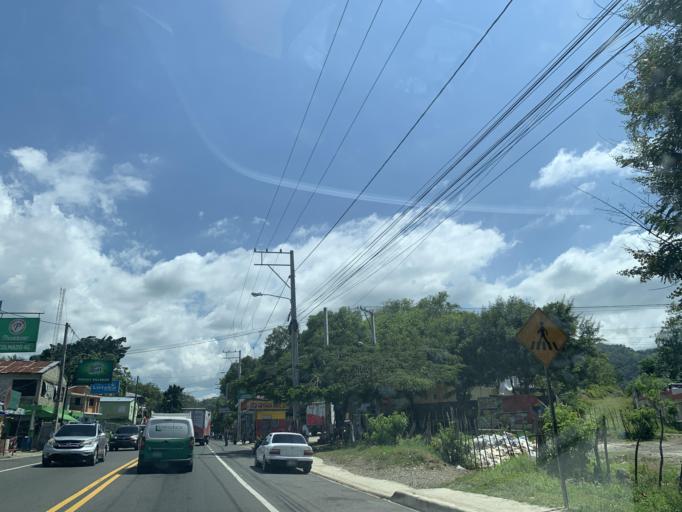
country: DO
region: Puerto Plata
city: Altamira
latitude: 19.7037
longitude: -70.8382
